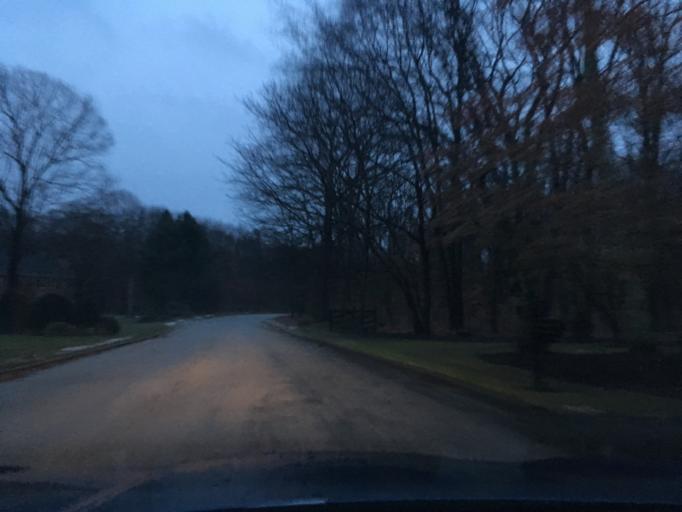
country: US
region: Rhode Island
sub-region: Kent County
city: West Warwick
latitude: 41.6530
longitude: -71.5131
